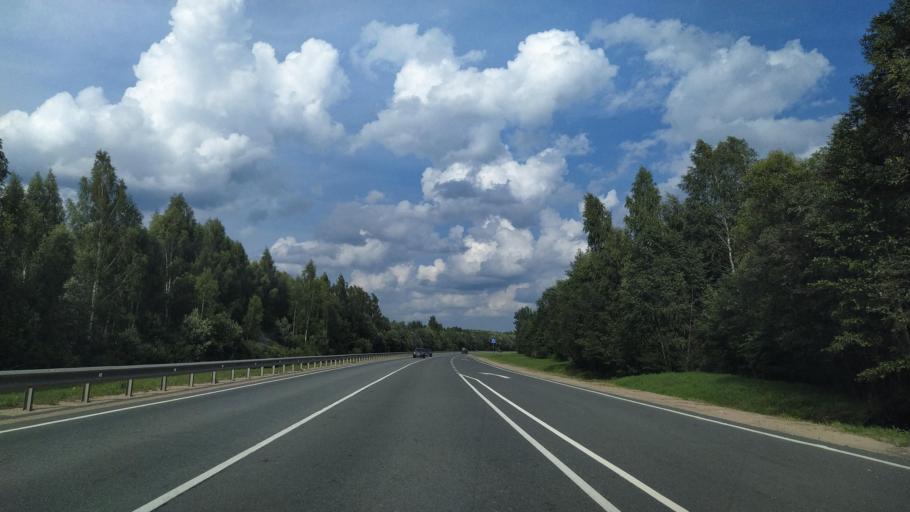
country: RU
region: Novgorod
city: Sol'tsy
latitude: 58.1609
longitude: 30.4511
